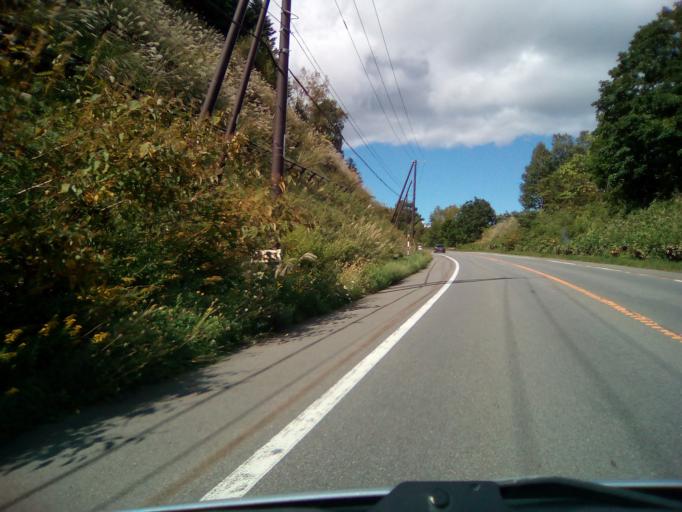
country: JP
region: Hokkaido
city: Date
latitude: 42.5859
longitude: 140.7938
